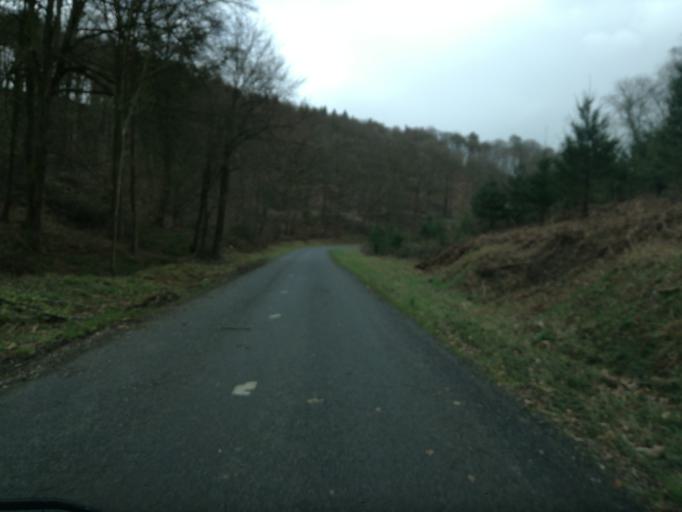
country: FR
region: Haute-Normandie
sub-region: Departement de la Seine-Maritime
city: Caudebec-en-Caux
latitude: 49.5583
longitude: 0.7431
